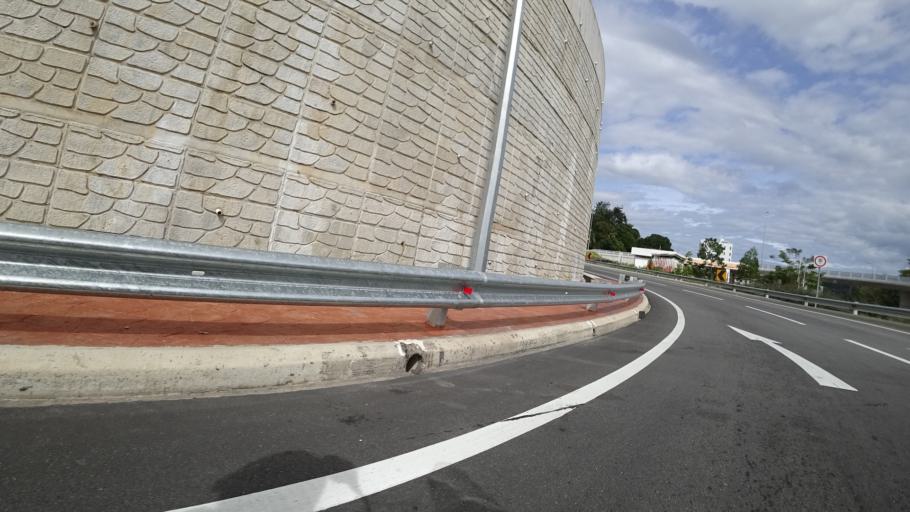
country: BN
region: Brunei and Muara
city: Bandar Seri Begawan
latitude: 4.8754
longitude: 114.9521
